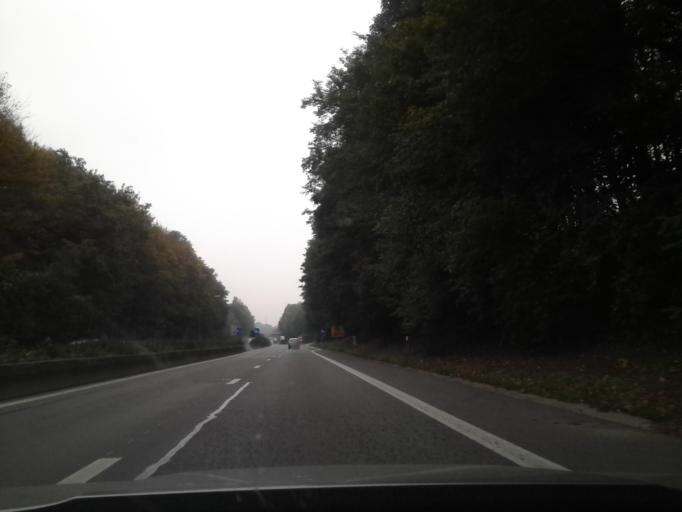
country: BE
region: Wallonia
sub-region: Province du Brabant Wallon
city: Tubize
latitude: 50.7065
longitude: 4.1803
